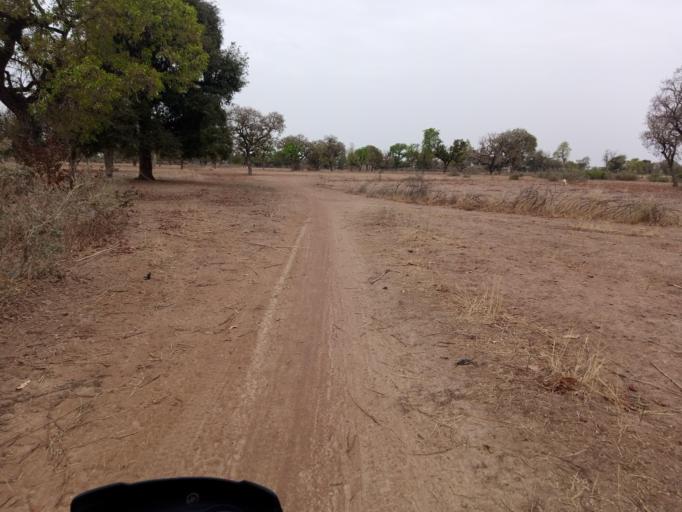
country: BF
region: Boucle du Mouhoun
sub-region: Province de la Kossi
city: Nouna
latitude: 12.7704
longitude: -4.0618
